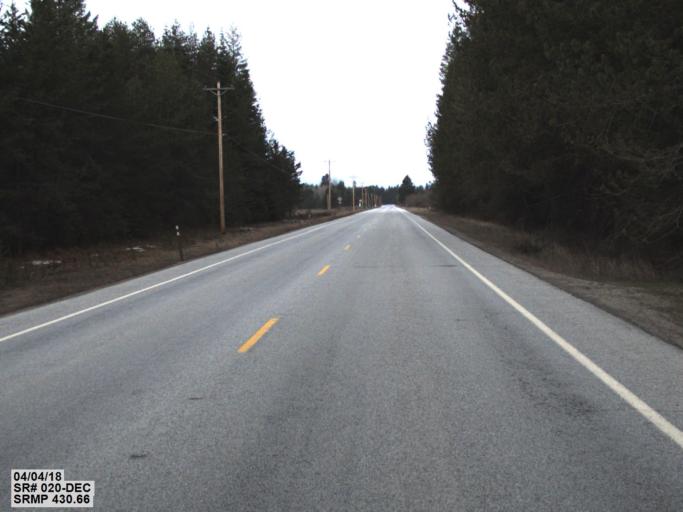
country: US
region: Washington
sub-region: Pend Oreille County
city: Newport
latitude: 48.2282
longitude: -117.1481
